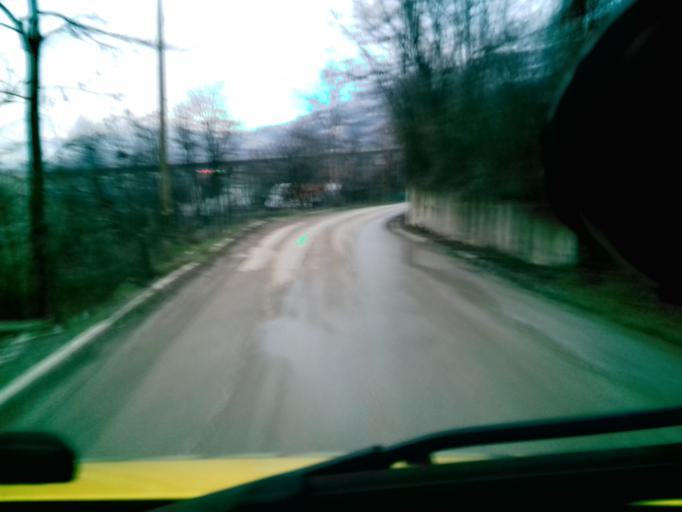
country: BA
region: Federation of Bosnia and Herzegovina
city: Zenica
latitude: 44.1766
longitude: 17.9757
